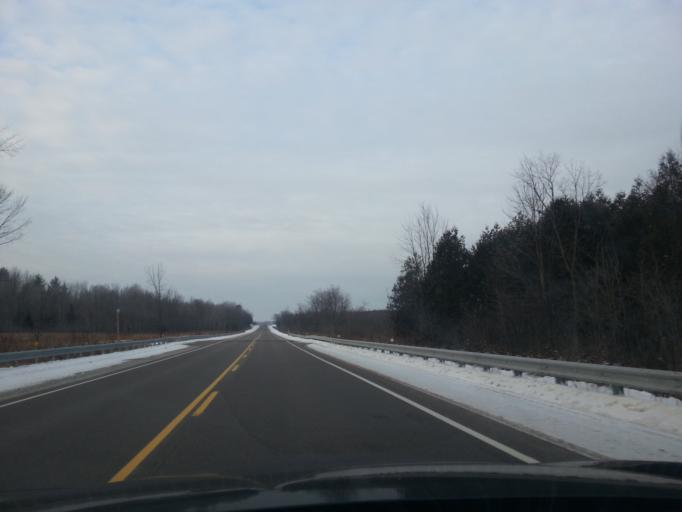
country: CA
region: Ontario
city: Perth
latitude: 44.8670
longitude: -76.3992
